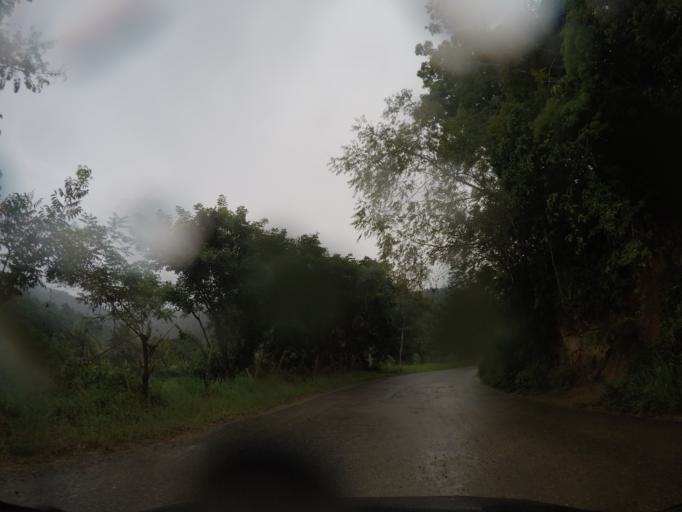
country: MX
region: Oaxaca
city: San Gabriel Mixtepec
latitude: 16.1065
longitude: -97.0639
